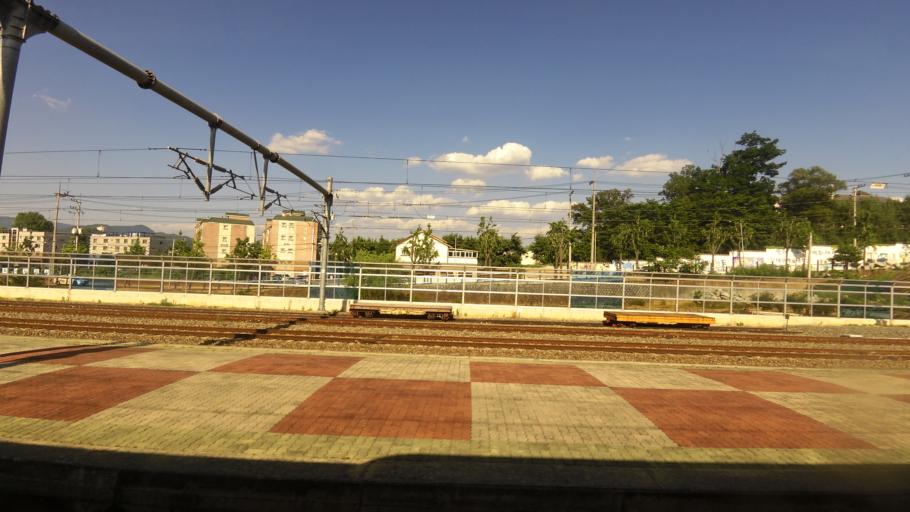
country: KR
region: Gyeongsangbuk-do
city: Waegwan
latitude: 35.9899
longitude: 128.4006
